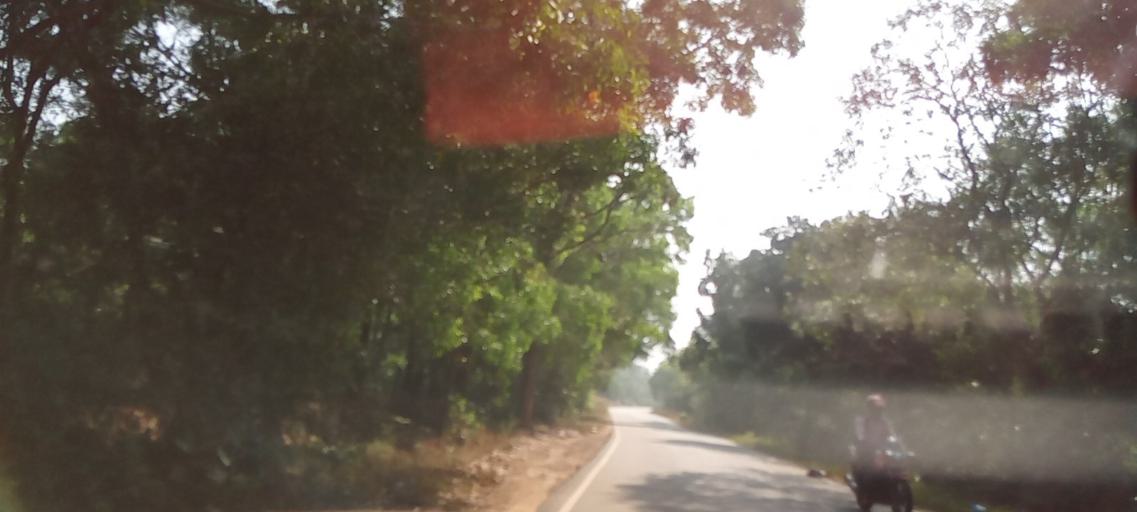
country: IN
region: Karnataka
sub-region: Udupi
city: Coondapoor
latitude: 13.5139
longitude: 74.7972
